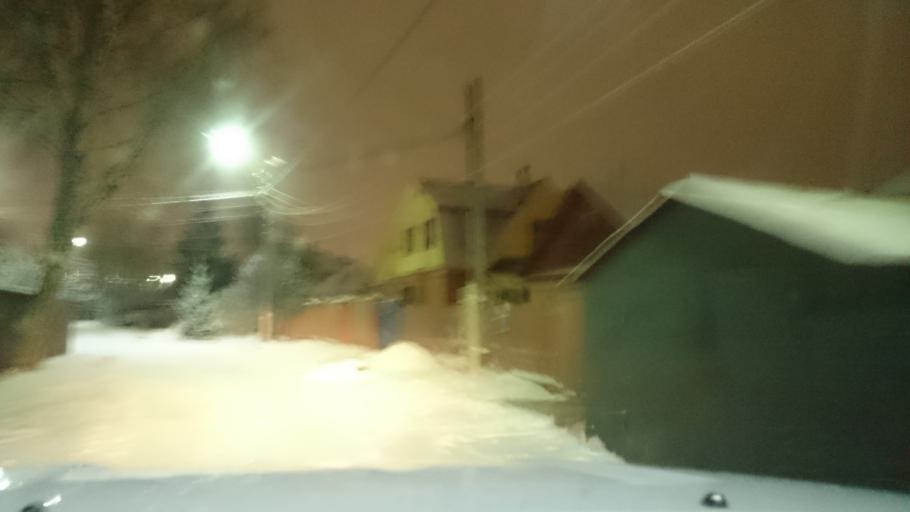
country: RU
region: Tula
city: Tula
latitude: 54.2020
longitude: 37.5639
